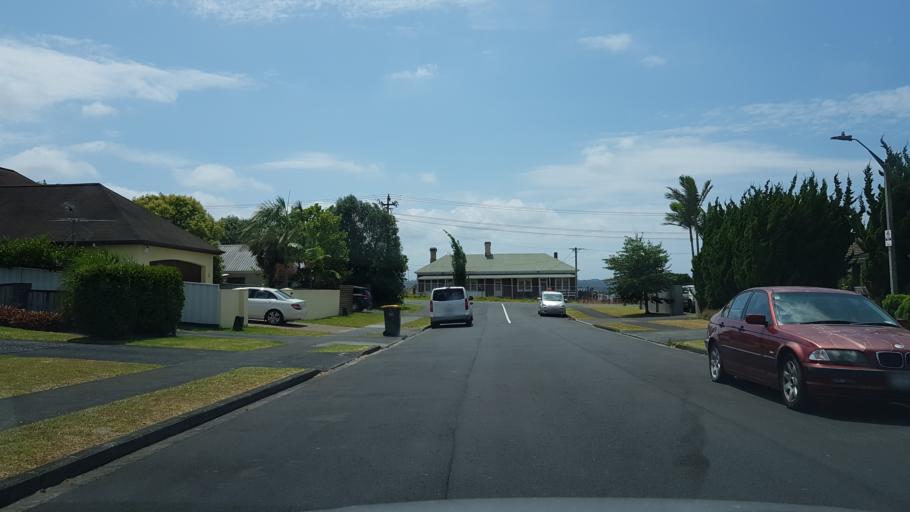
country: NZ
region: Auckland
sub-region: Auckland
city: Rosebank
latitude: -36.7993
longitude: 174.6498
